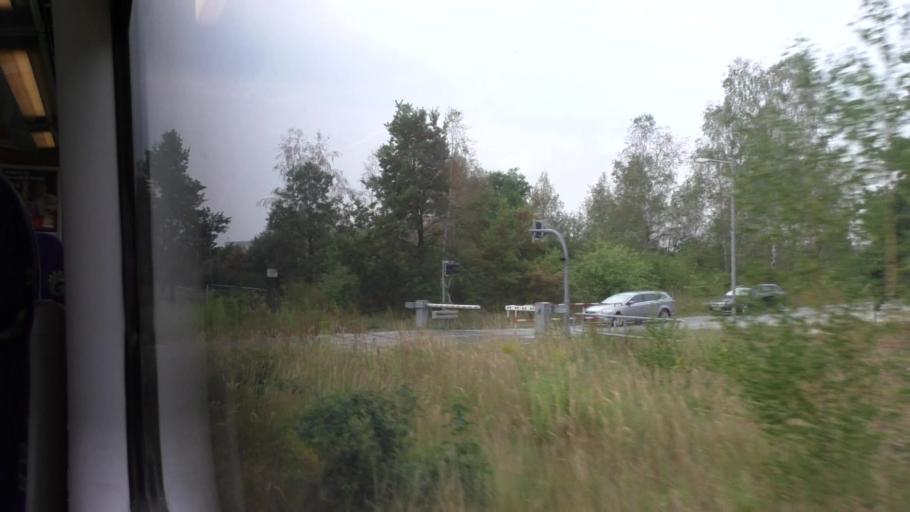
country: DE
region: Saxony
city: Ostritz
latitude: 51.0666
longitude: 14.9582
